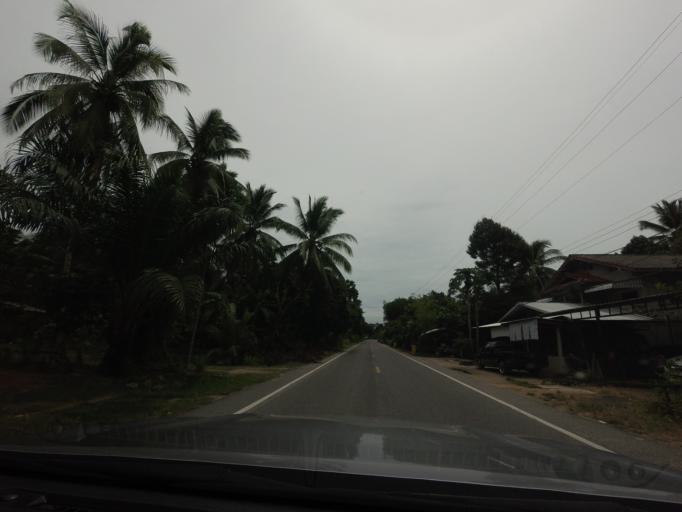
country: TH
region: Pattani
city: Kapho
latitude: 6.6300
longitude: 101.5477
